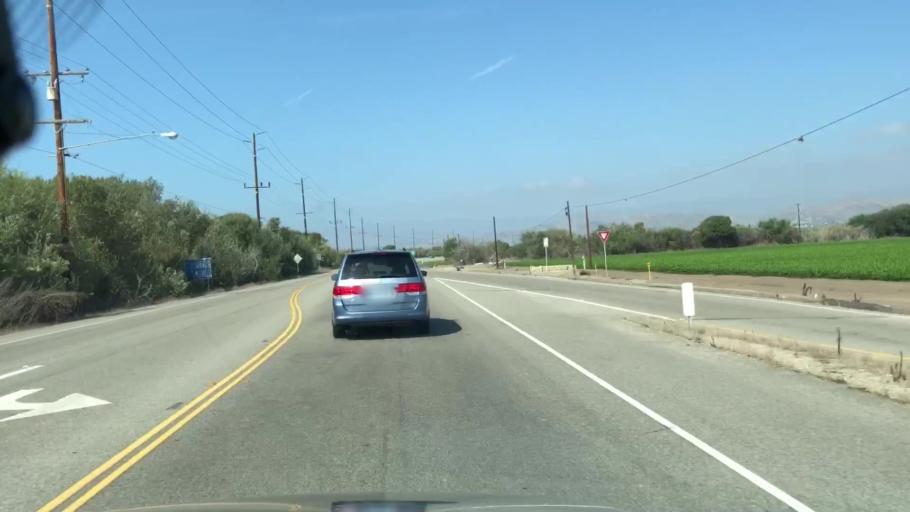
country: US
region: California
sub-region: Ventura County
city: Oxnard Shores
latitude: 34.2192
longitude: -119.2541
